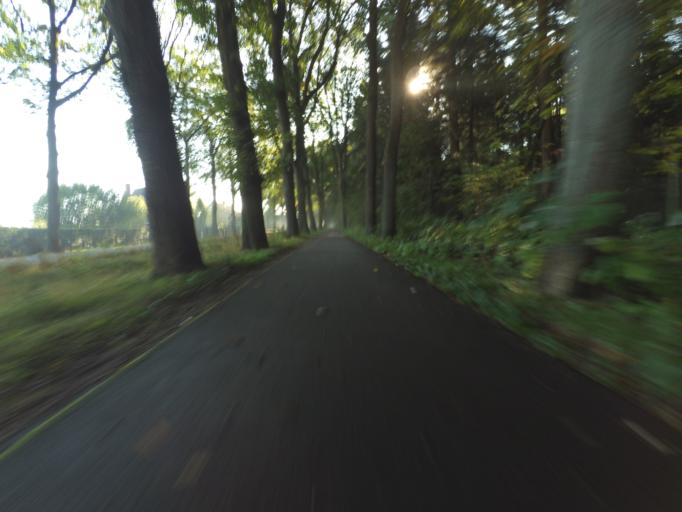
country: NL
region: Gelderland
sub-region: Gemeente Apeldoorn
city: Apeldoorn
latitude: 52.2435
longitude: 5.9511
